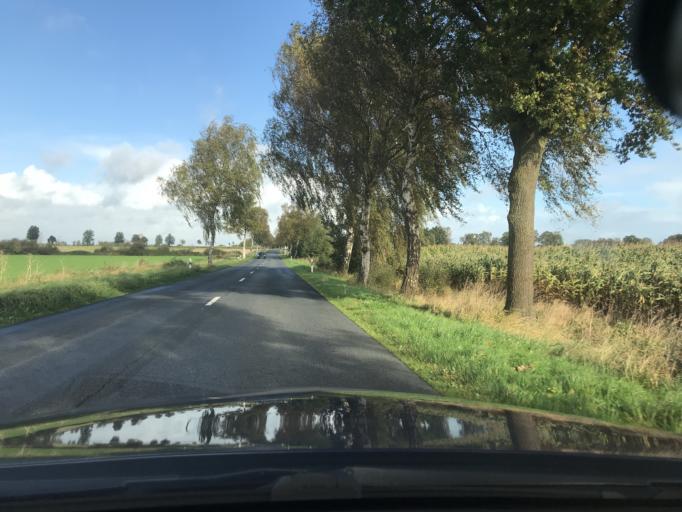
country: DE
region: Lower Saxony
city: Ahlerstedt
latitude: 53.4262
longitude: 9.4612
